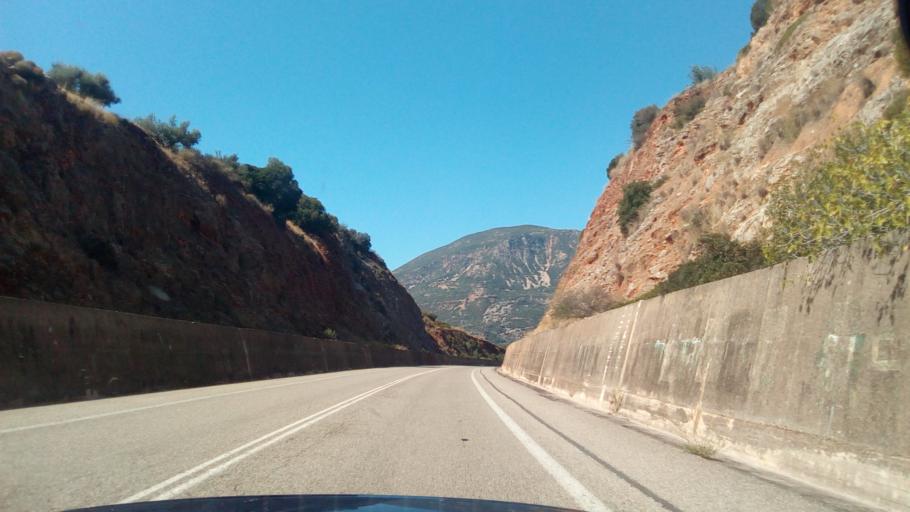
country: GR
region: West Greece
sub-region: Nomos Achaias
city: Selianitika
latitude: 38.3889
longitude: 22.0772
